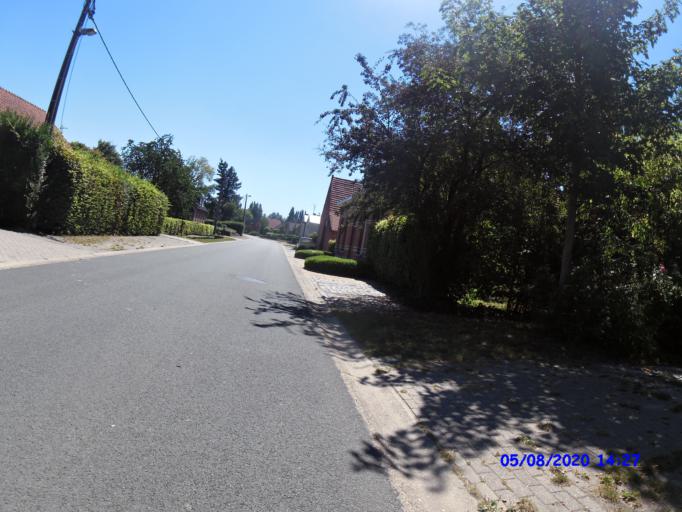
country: BE
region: Flanders
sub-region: Provincie Antwerpen
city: Hoogstraten
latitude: 51.3784
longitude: 4.7687
